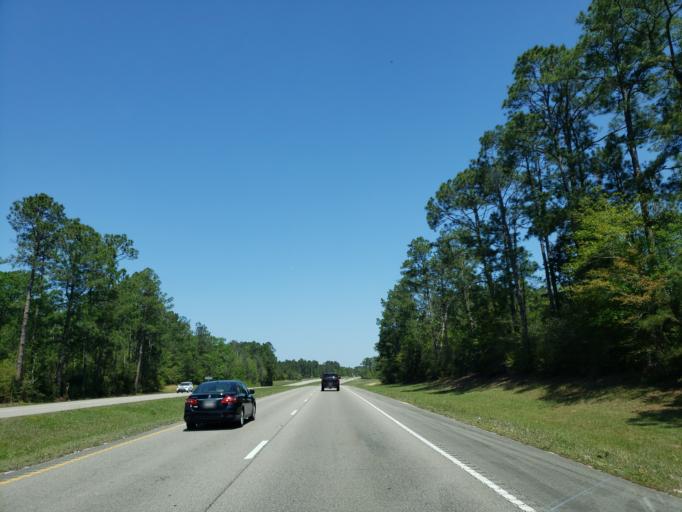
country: US
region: Mississippi
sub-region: Harrison County
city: Saucier
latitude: 30.6411
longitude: -89.1322
